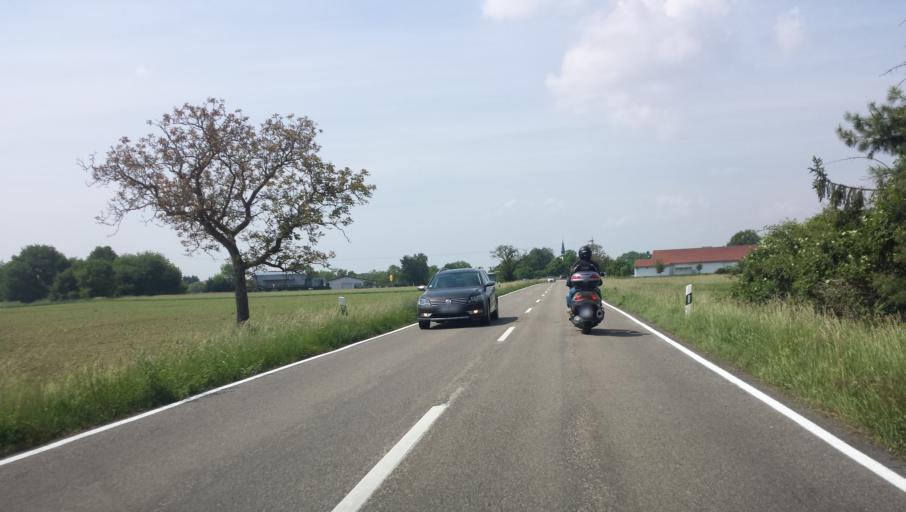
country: DE
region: Rheinland-Pfalz
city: Berg
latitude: 48.9814
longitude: 8.1893
